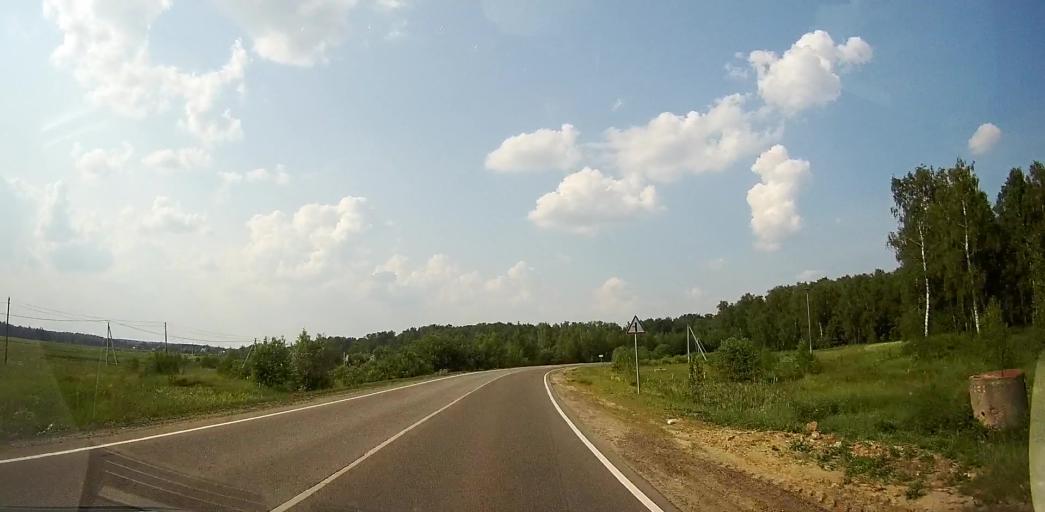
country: RU
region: Moskovskaya
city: Mikhnevo
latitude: 55.1629
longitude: 37.9594
